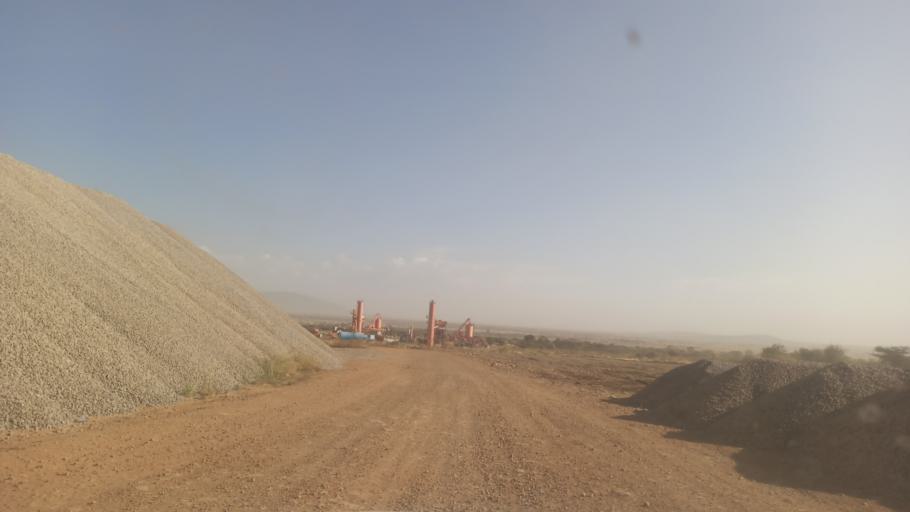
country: ET
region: Oromiya
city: Ziway
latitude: 7.9336
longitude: 38.6153
